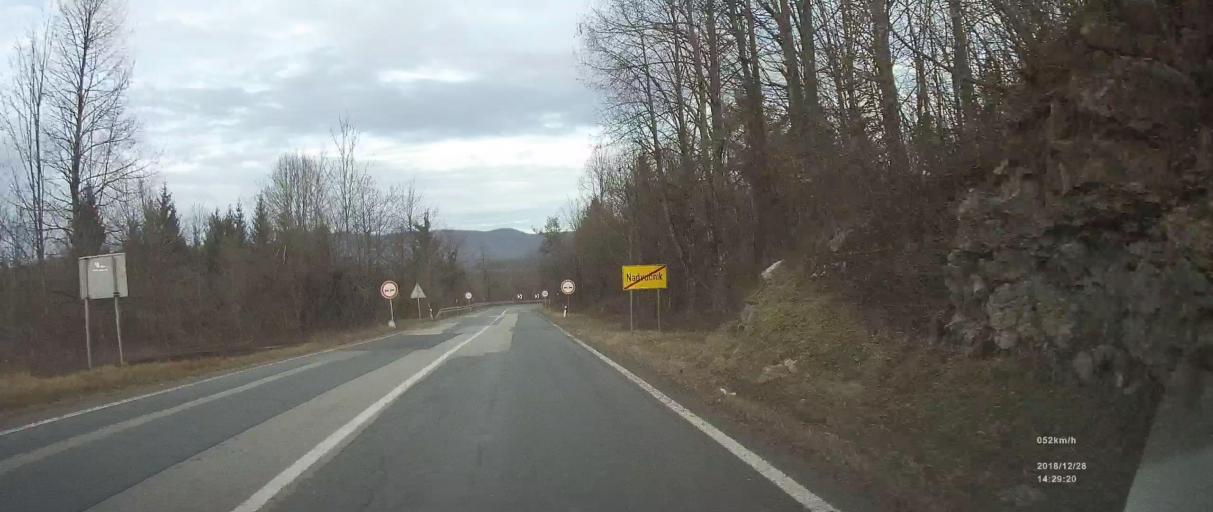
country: HR
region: Primorsko-Goranska
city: Vrbovsko
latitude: 45.4192
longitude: 15.1161
